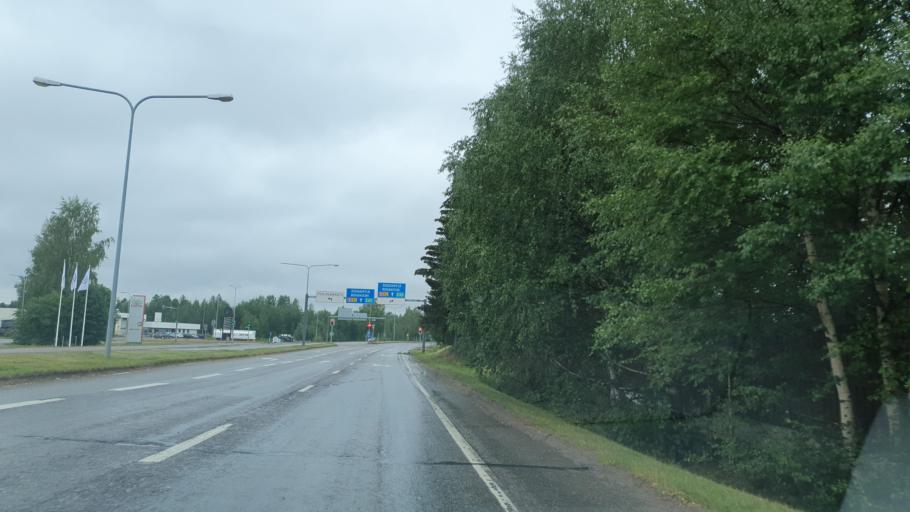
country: FI
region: Lapland
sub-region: Itae-Lappi
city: Kemijaervi
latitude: 66.7186
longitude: 27.4177
